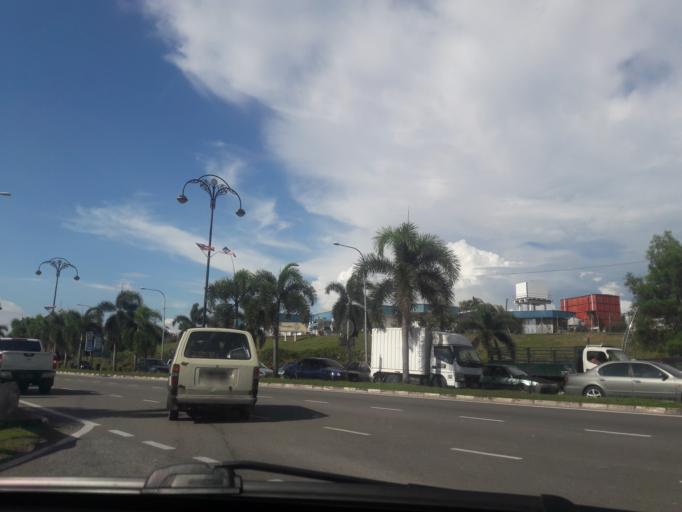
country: MY
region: Kedah
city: Sungai Petani
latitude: 5.6155
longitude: 100.4730
